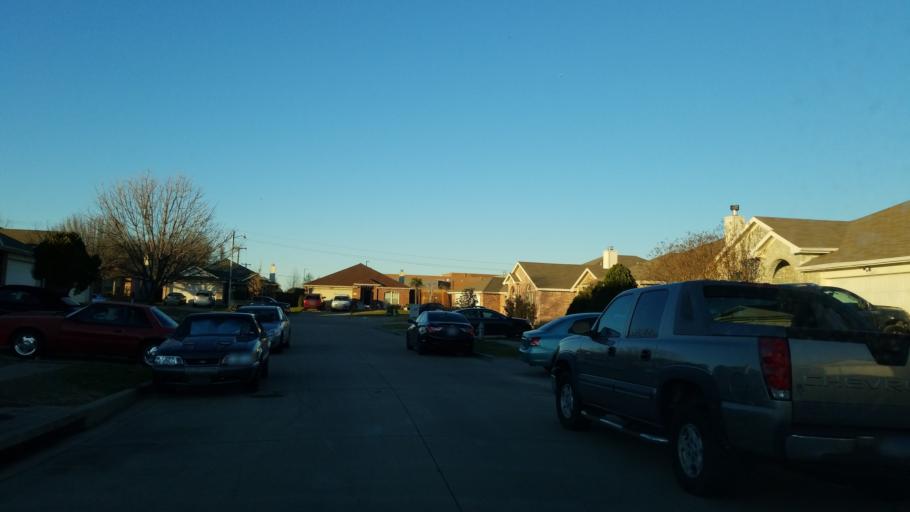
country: US
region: Texas
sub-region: Dallas County
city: Grand Prairie
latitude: 32.7270
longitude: -97.0512
